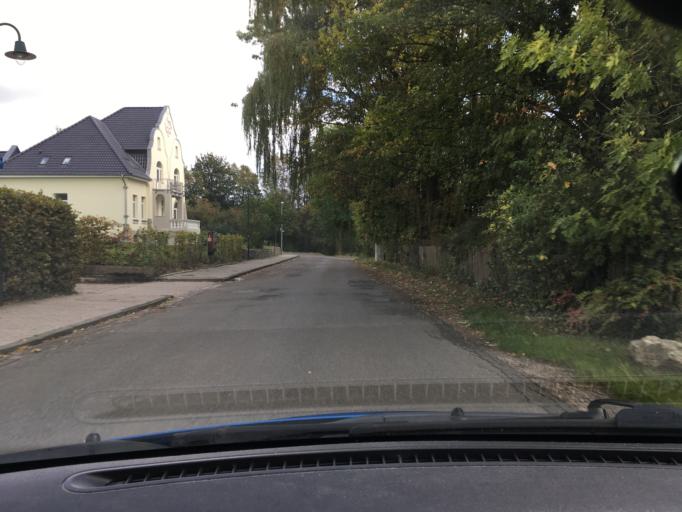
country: DE
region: Lower Saxony
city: Bad Munder am Deister
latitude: 52.2065
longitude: 9.4726
